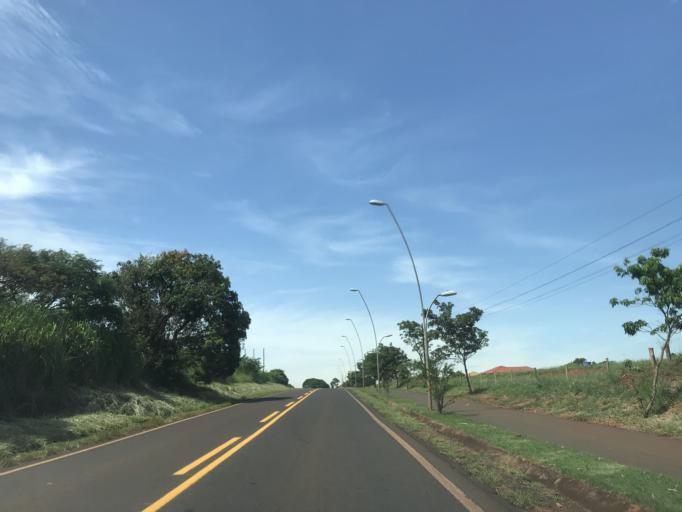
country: BR
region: Parana
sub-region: Terra Rica
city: Terra Rica
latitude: -22.7472
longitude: -52.6251
